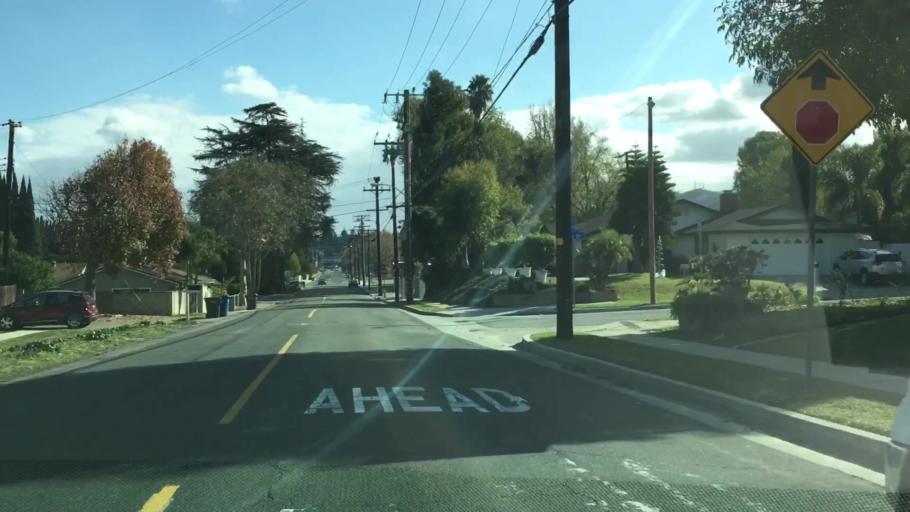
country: US
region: California
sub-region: Los Angeles County
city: Hacienda Heights
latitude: 33.9983
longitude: -117.9755
